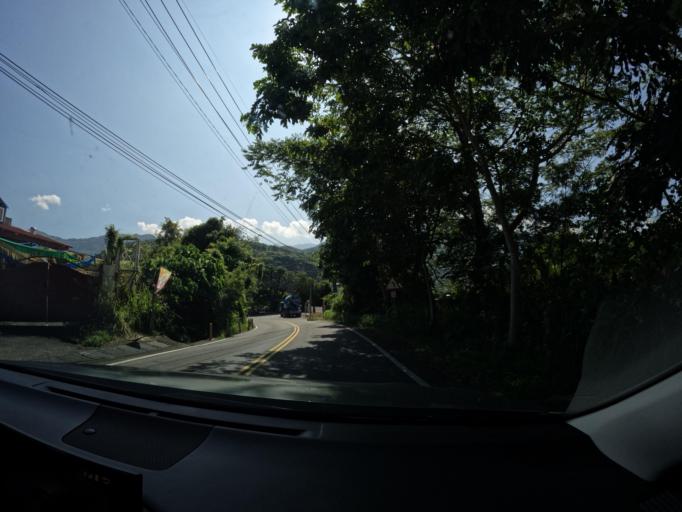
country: TW
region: Taiwan
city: Yujing
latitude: 23.1018
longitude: 120.6886
